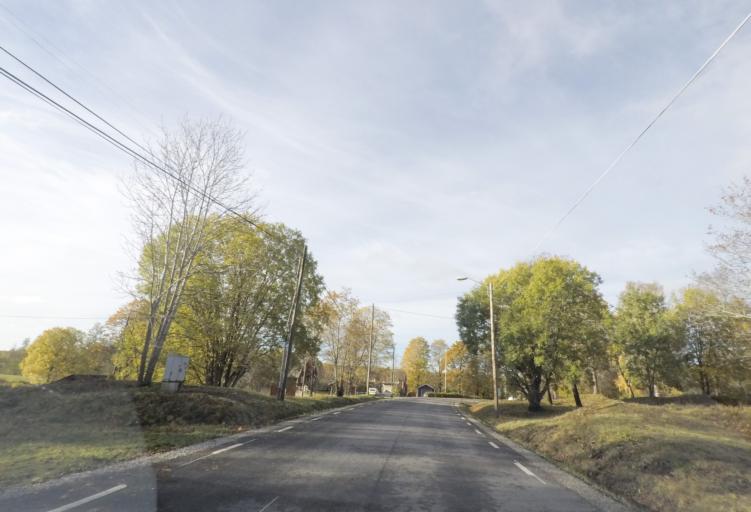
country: SE
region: OErebro
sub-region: Lindesbergs Kommun
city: Stora
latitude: 59.8030
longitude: 15.1645
